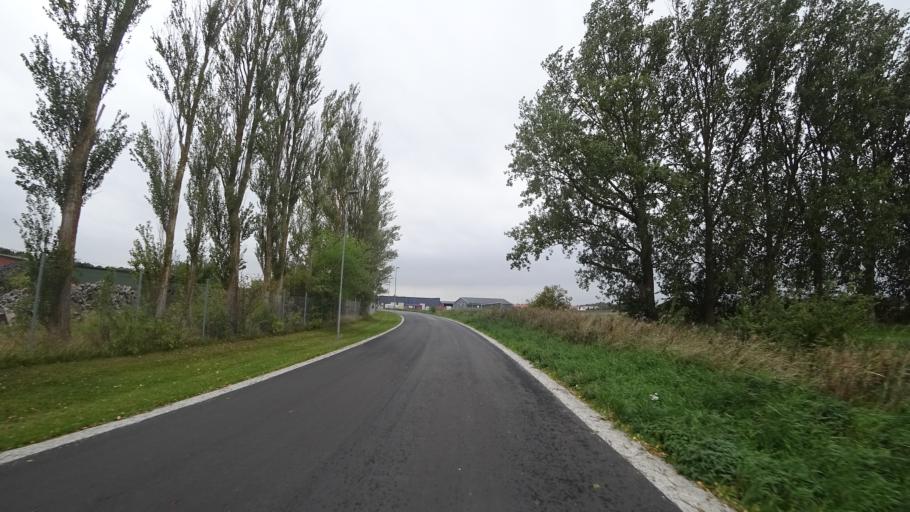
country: SE
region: Skane
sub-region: Kavlinge Kommun
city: Kaevlinge
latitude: 55.8000
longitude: 13.1255
